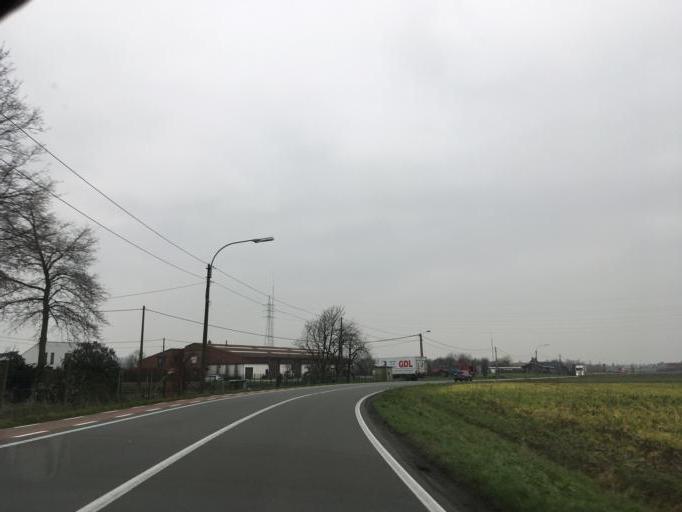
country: BE
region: Flanders
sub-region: Provincie West-Vlaanderen
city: Ardooie
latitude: 50.9672
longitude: 3.2297
